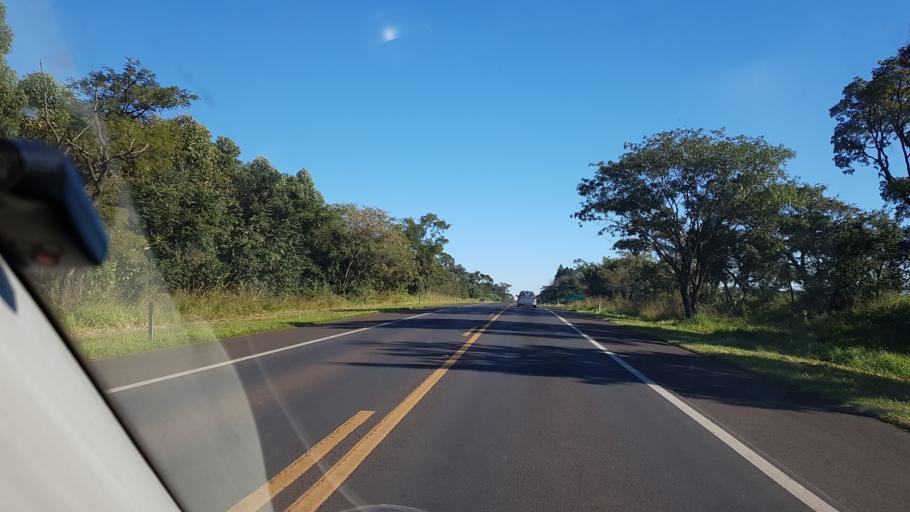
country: BR
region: Sao Paulo
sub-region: Assis
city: Assis
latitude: -22.6239
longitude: -50.4495
